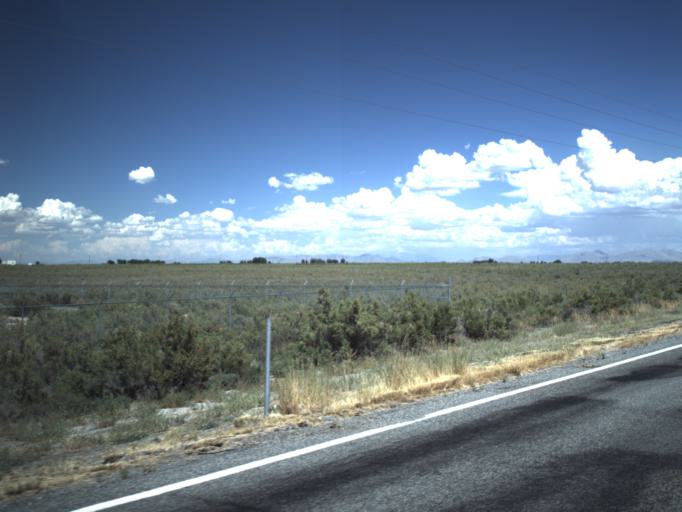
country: US
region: Utah
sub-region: Millard County
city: Delta
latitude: 39.3309
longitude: -112.7072
